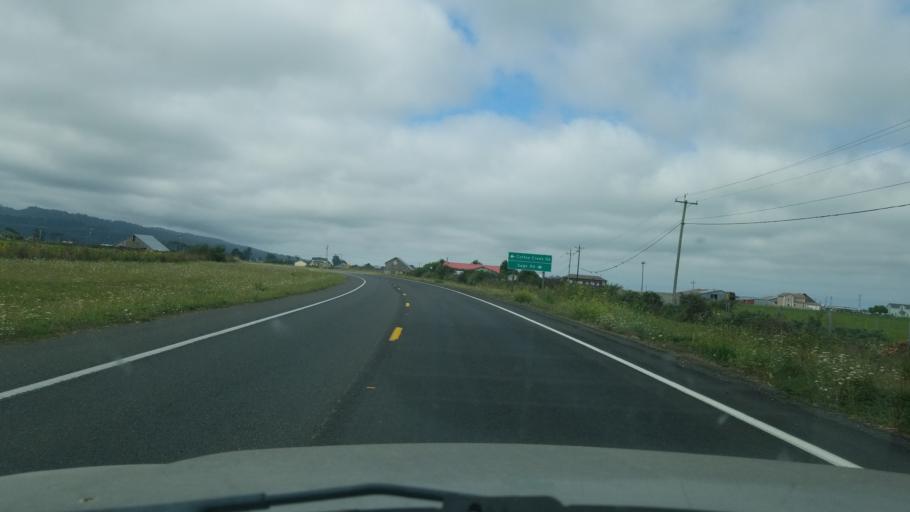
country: US
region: California
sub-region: Humboldt County
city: Ferndale
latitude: 40.5990
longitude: -124.2264
